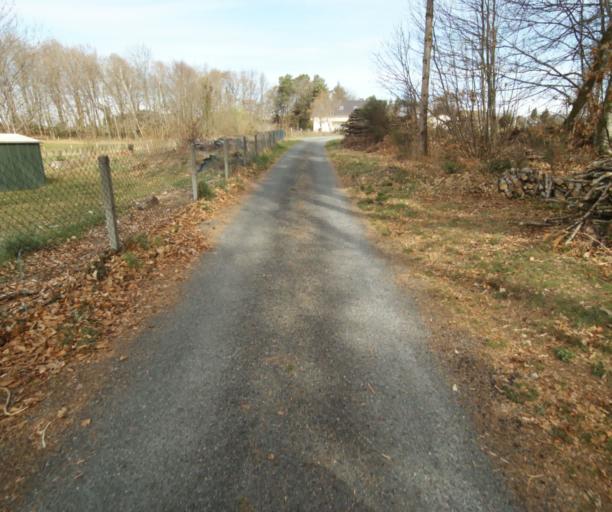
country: FR
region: Limousin
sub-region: Departement de la Correze
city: Correze
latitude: 45.4171
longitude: 1.8301
